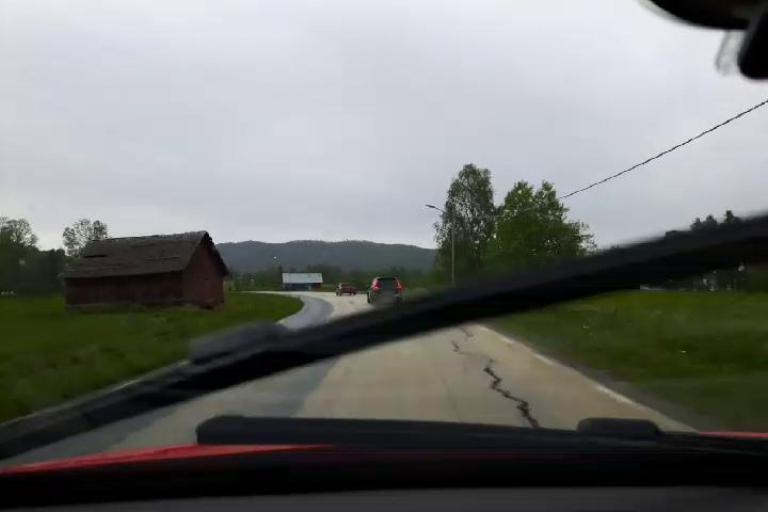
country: SE
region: Jaemtland
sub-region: Bergs Kommun
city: Hoverberg
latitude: 62.7978
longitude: 14.4392
